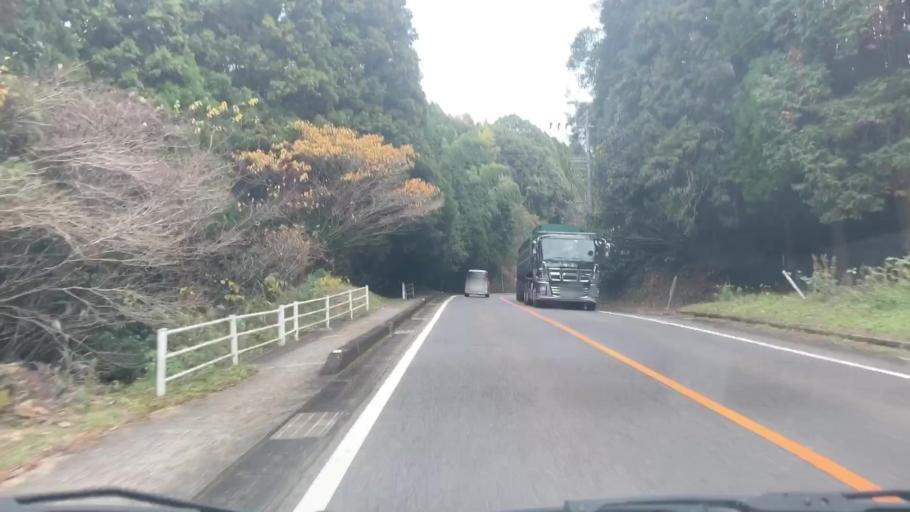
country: JP
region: Saga Prefecture
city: Ureshinomachi-shimojuku
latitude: 33.1614
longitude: 129.9679
